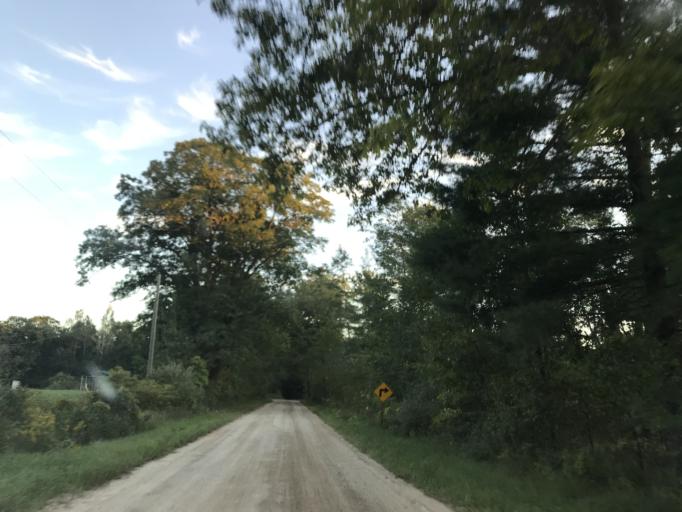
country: US
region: Michigan
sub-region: Mason County
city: Scottville
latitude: 43.9196
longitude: -86.1688
